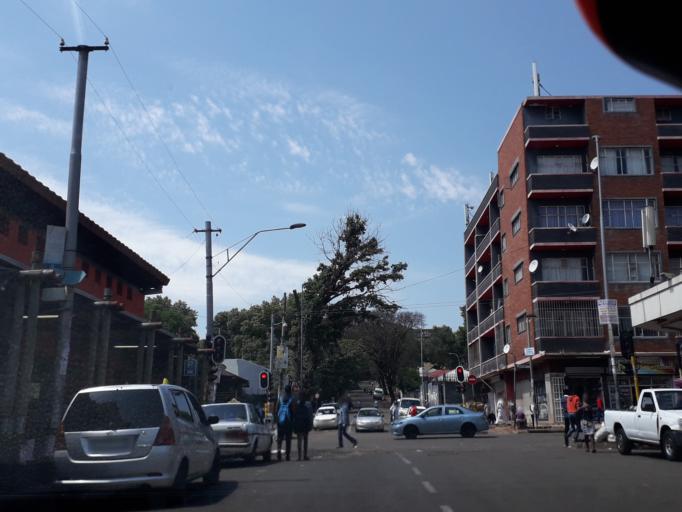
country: ZA
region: Gauteng
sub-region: City of Johannesburg Metropolitan Municipality
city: Johannesburg
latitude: -26.1809
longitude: 28.0648
